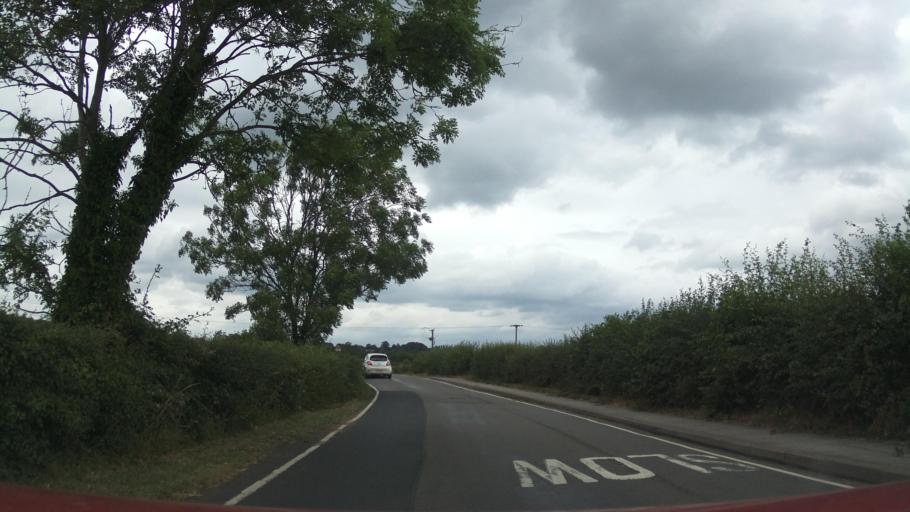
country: GB
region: England
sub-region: Derbyshire
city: Long Eaton
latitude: 52.9060
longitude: -1.3190
